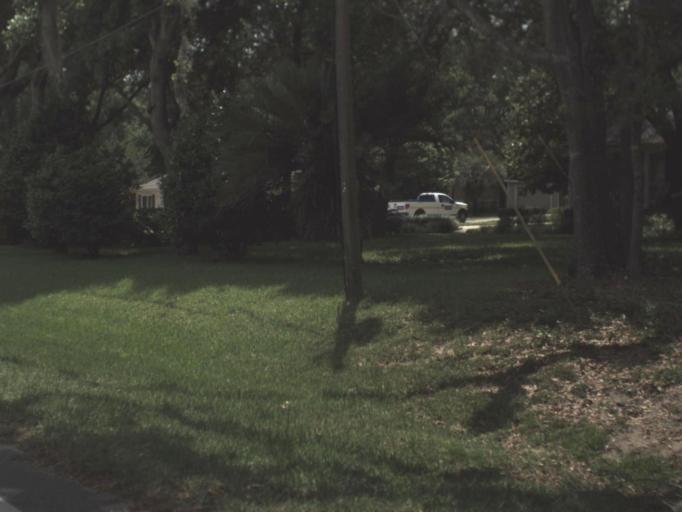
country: US
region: Florida
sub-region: Clay County
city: Keystone Heights
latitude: 29.7734
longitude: -82.0353
